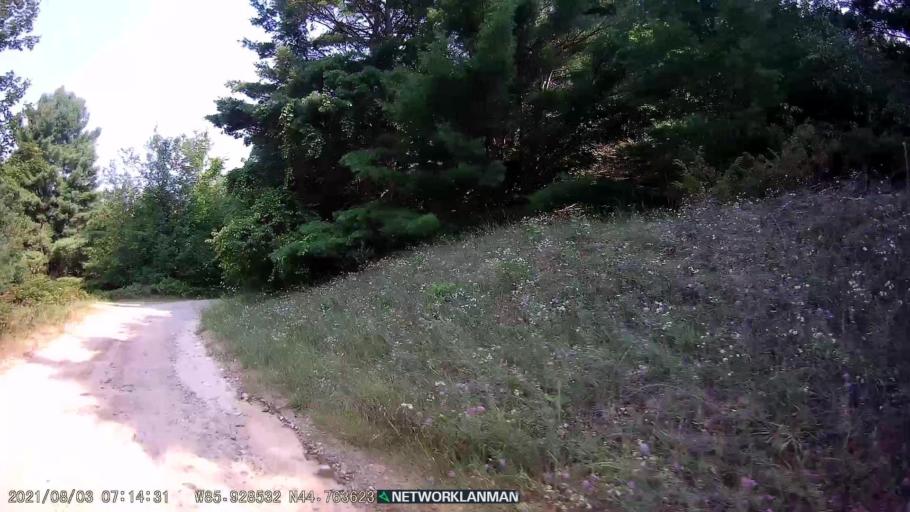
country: US
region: Michigan
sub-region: Benzie County
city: Beulah
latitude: 44.7637
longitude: -85.9285
